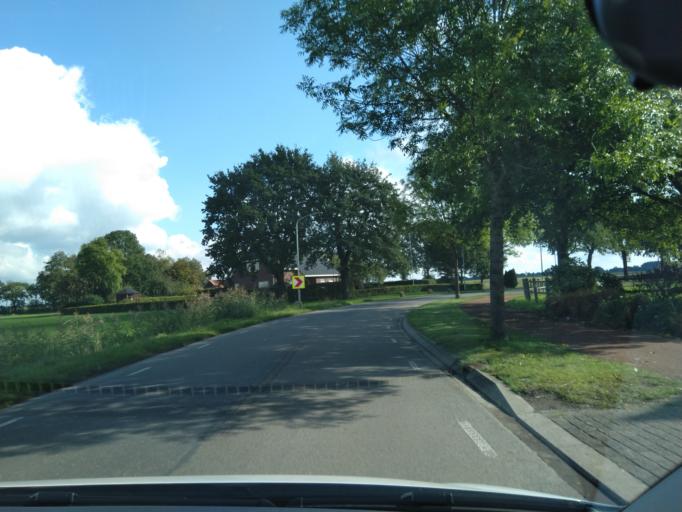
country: NL
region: Groningen
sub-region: Gemeente Pekela
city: Oude Pekela
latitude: 53.0954
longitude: 6.9575
